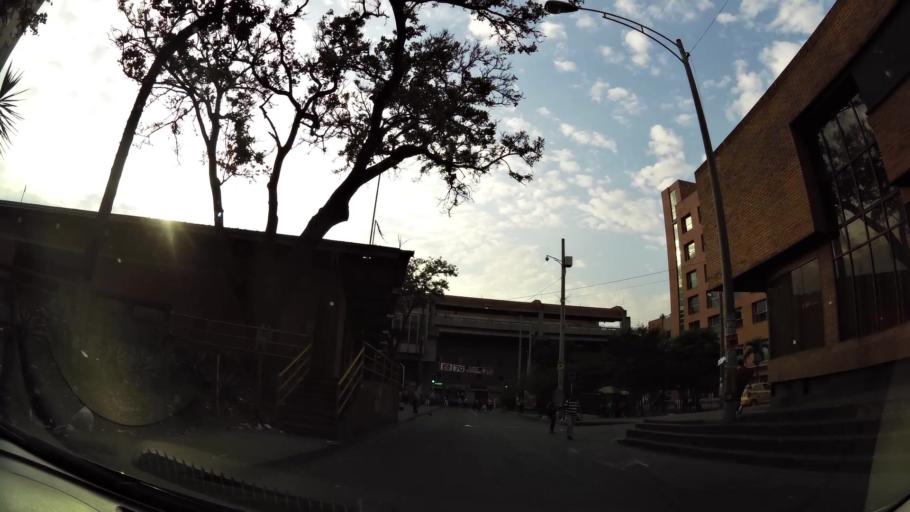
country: CO
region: Antioquia
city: Medellin
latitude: 6.2569
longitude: -75.5654
